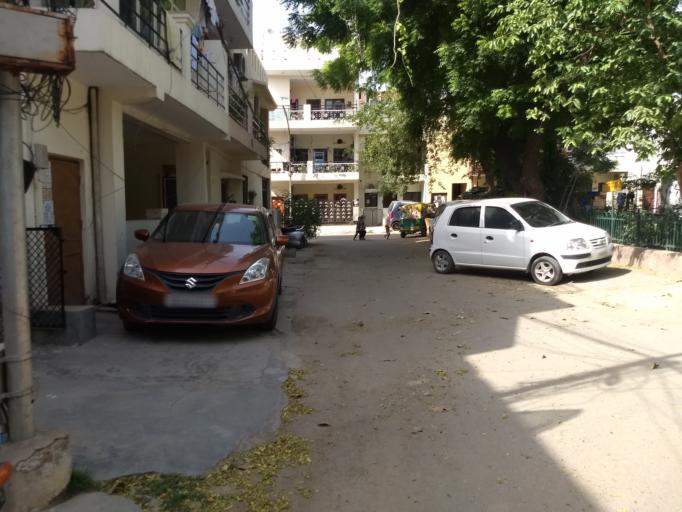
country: IN
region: Haryana
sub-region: Gurgaon
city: Gurgaon
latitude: 28.4743
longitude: 77.0805
